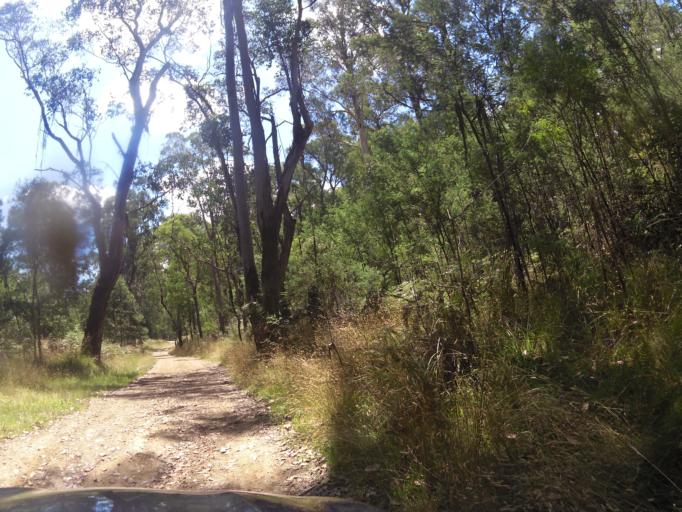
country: AU
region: Victoria
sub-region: Alpine
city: Mount Beauty
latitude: -36.7806
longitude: 147.0680
